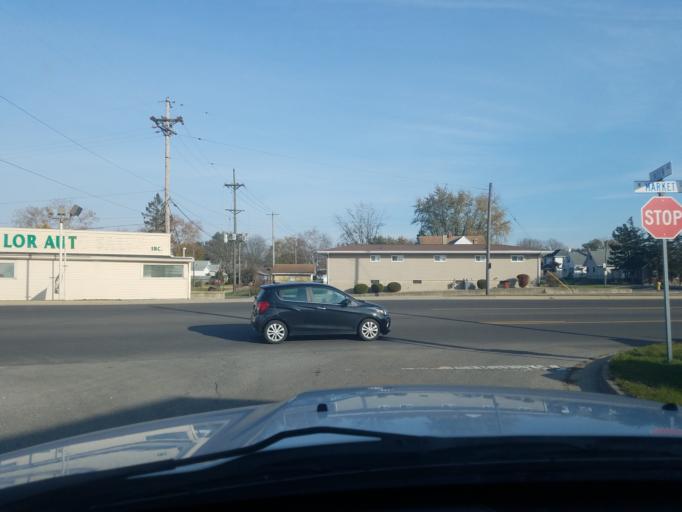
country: US
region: Indiana
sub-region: Cass County
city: Dunkirk
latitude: 40.7553
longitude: -86.3832
